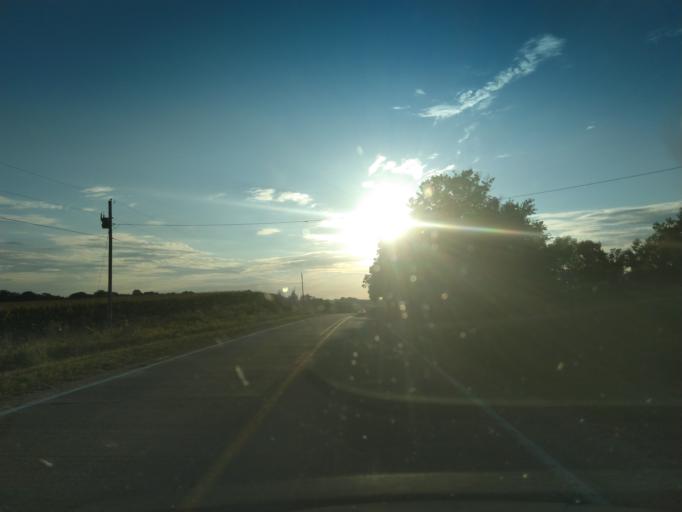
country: US
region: Iowa
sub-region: Jackson County
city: Maquoketa
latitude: 42.1641
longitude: -90.7020
